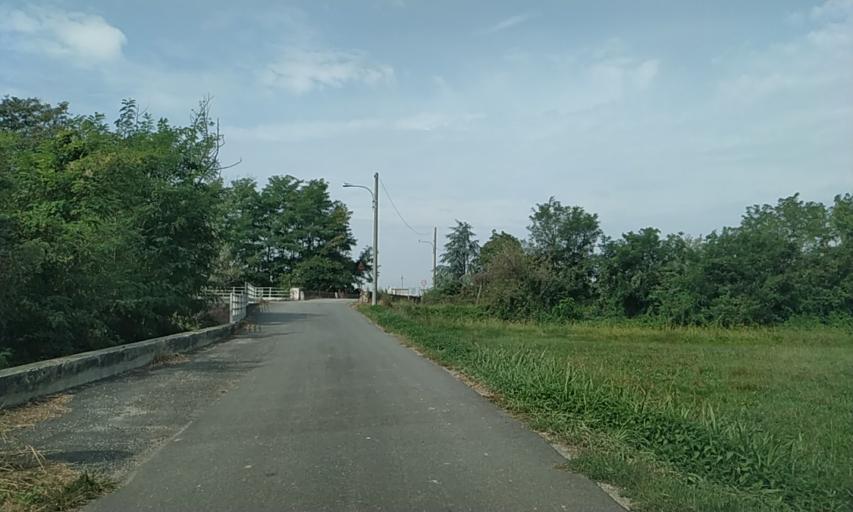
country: IT
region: Piedmont
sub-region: Provincia di Vercelli
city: Livorno Ferraris
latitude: 45.3086
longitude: 8.0823
